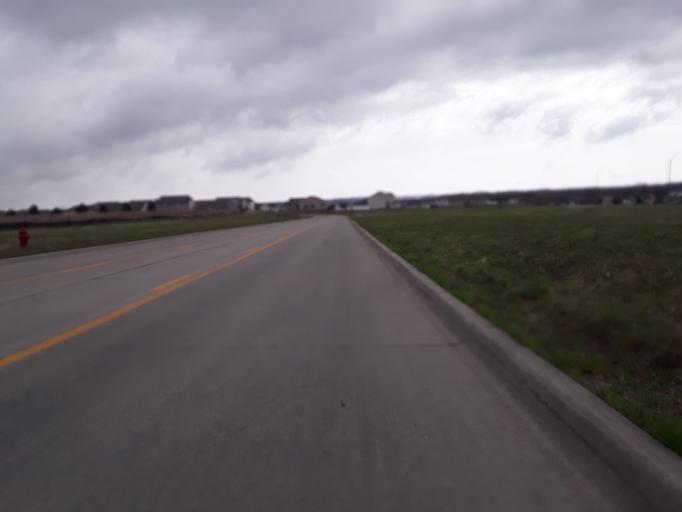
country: US
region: Nebraska
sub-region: Lancaster County
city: Lincoln
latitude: 40.8435
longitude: -96.6040
